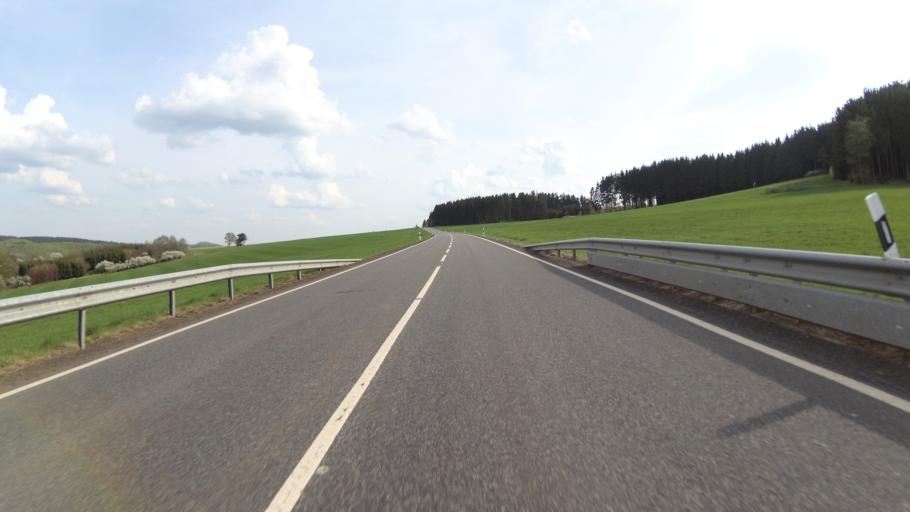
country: DE
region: Rheinland-Pfalz
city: Katzwinkel
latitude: 50.2607
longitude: 6.9203
